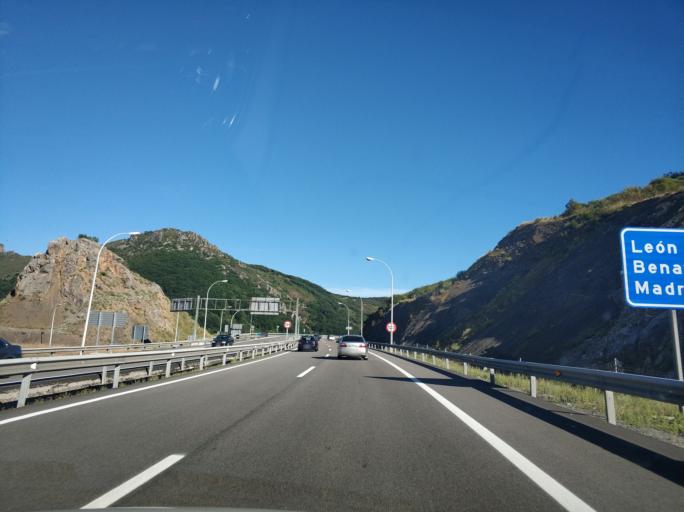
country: ES
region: Castille and Leon
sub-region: Provincia de Leon
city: Sena de Luna
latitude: 42.9084
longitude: -5.8924
